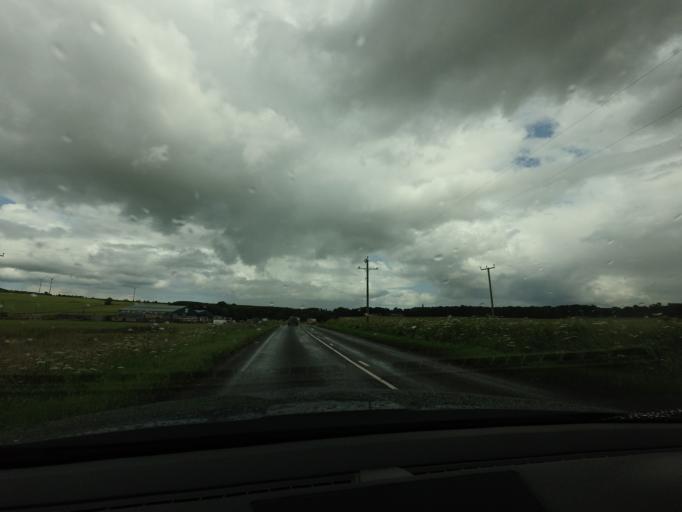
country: GB
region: Scotland
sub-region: Aberdeenshire
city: Turriff
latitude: 57.5519
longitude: -2.4416
